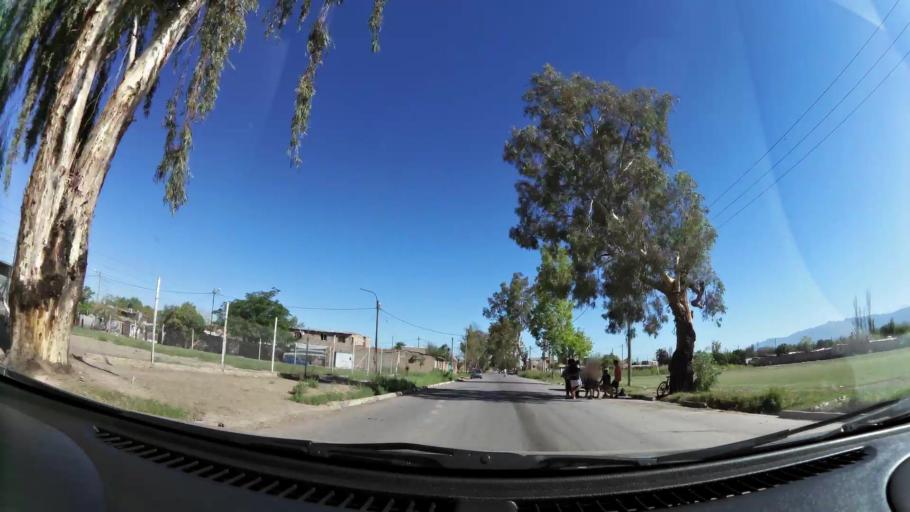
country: AR
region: Mendoza
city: Las Heras
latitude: -32.8285
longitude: -68.8162
